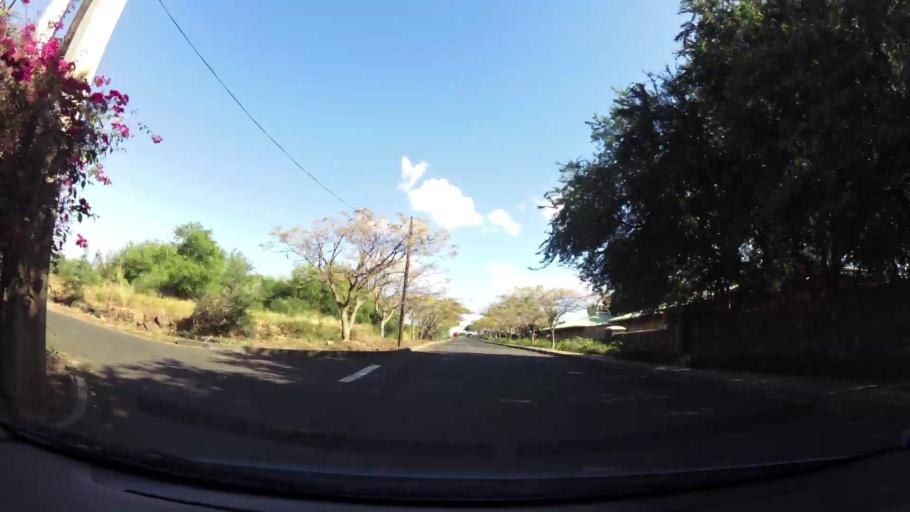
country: MU
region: Black River
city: Albion
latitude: -20.2183
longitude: 57.4012
